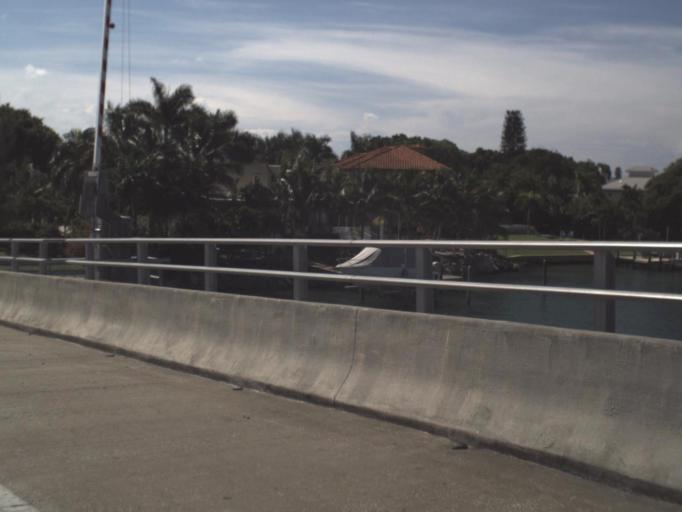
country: US
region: Florida
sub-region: Sarasota County
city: Siesta Key
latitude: 27.3327
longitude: -82.5815
